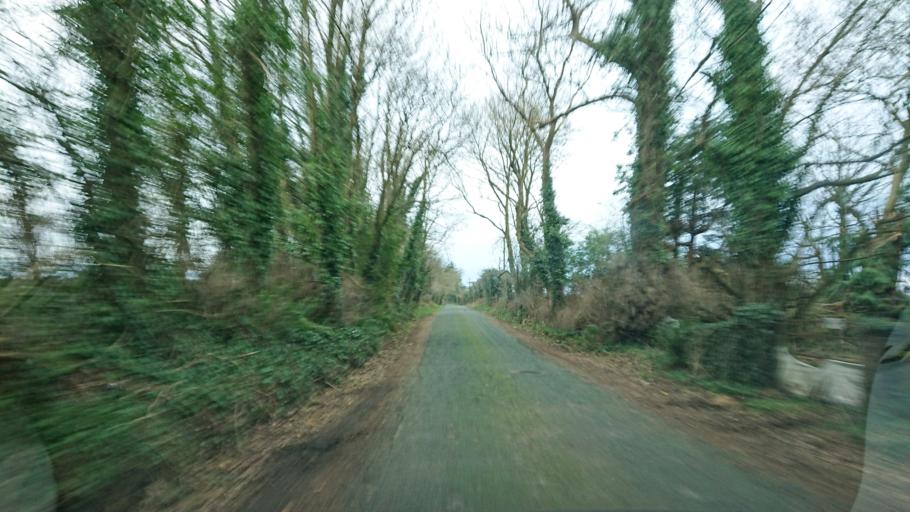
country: IE
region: Leinster
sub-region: Kilkenny
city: Mooncoin
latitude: 52.2256
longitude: -7.2660
